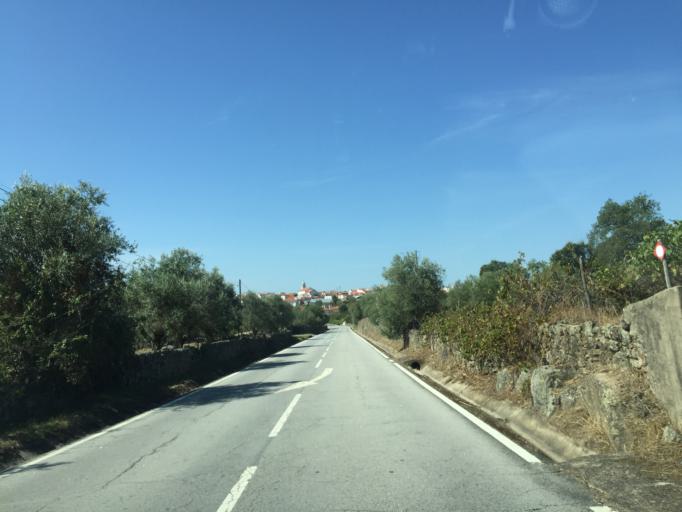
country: PT
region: Portalegre
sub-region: Portalegre
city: Alagoa
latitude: 39.4201
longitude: -7.6111
